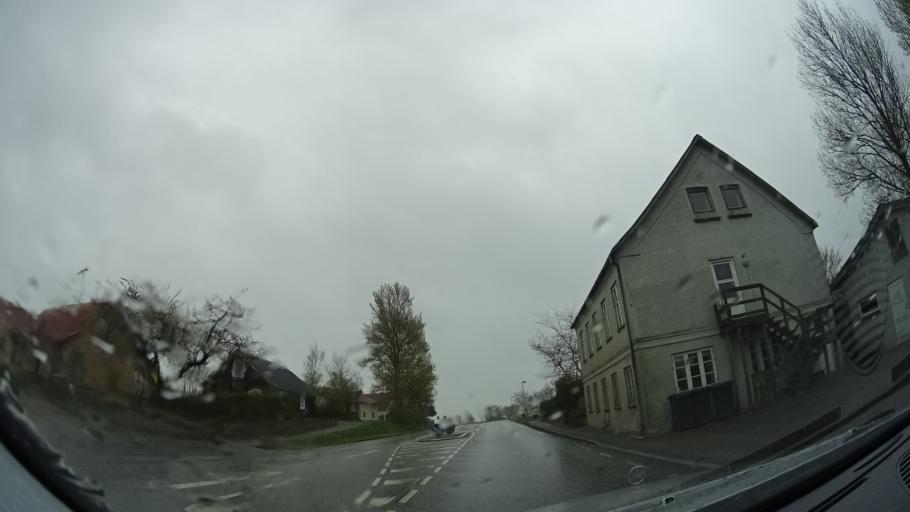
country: DK
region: Zealand
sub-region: Odsherred Kommune
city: Asnaes
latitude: 55.8058
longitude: 11.5967
